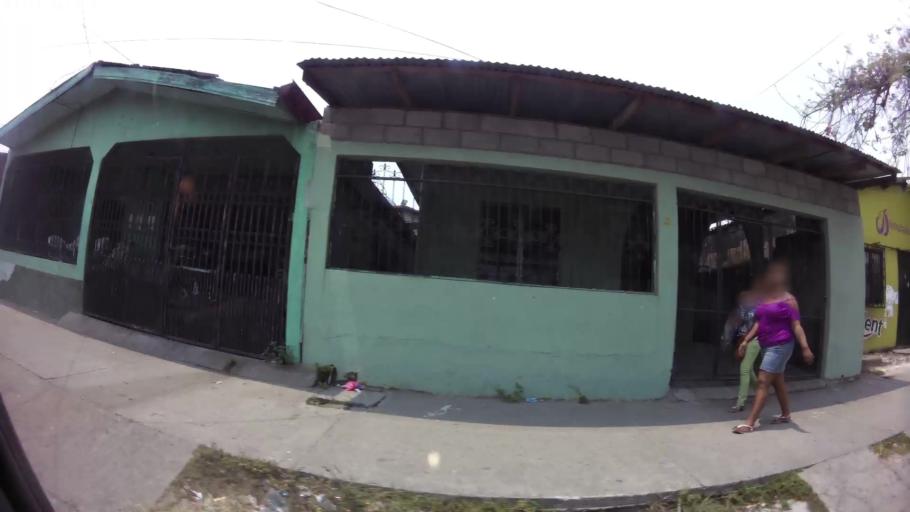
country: HN
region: Cortes
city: San Pedro Sula
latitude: 15.4911
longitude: -88.0168
